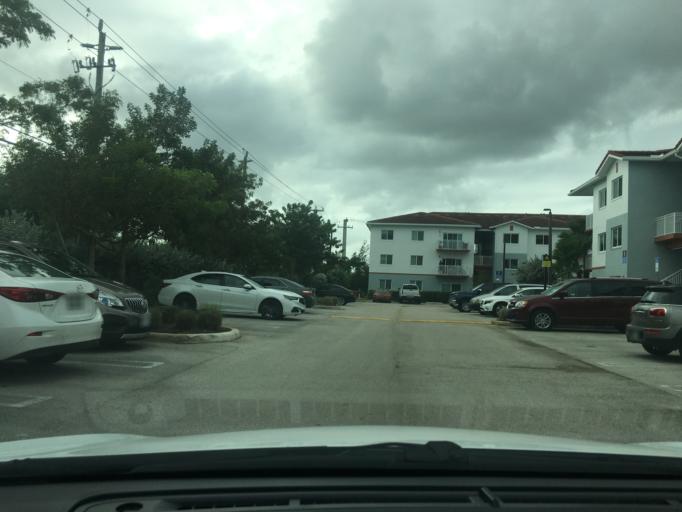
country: US
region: Florida
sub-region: Miami-Dade County
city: Biscayne Park
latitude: 25.8865
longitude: -80.1691
